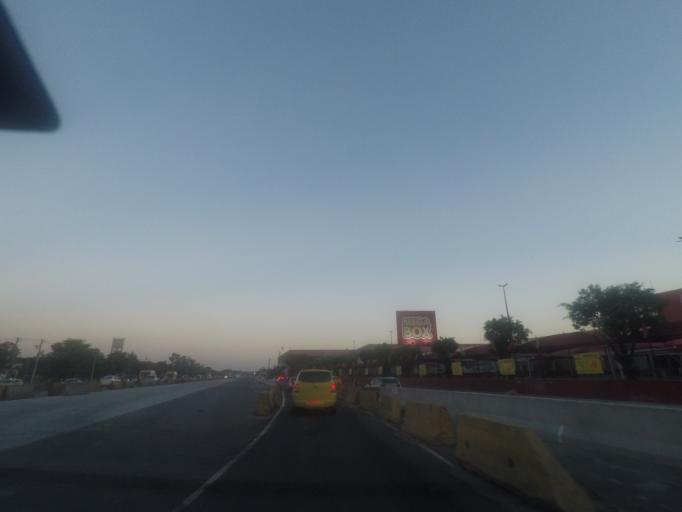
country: BR
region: Rio de Janeiro
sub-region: Duque De Caxias
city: Duque de Caxias
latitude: -22.8341
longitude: -43.2636
